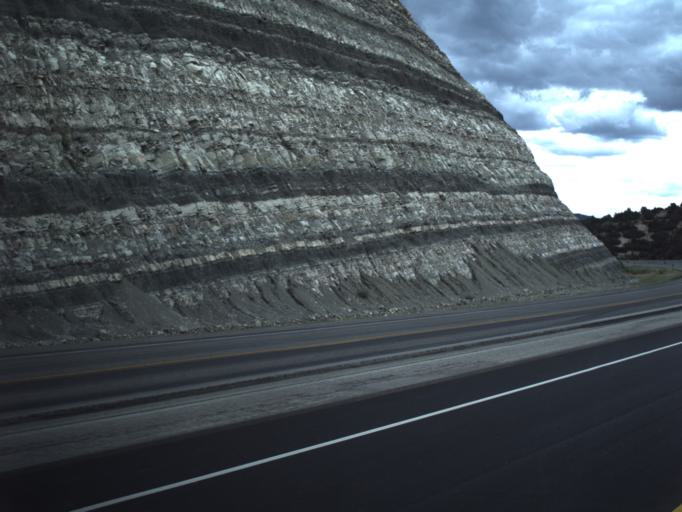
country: US
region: Utah
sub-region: Utah County
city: Mapleton
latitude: 39.9535
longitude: -111.2630
